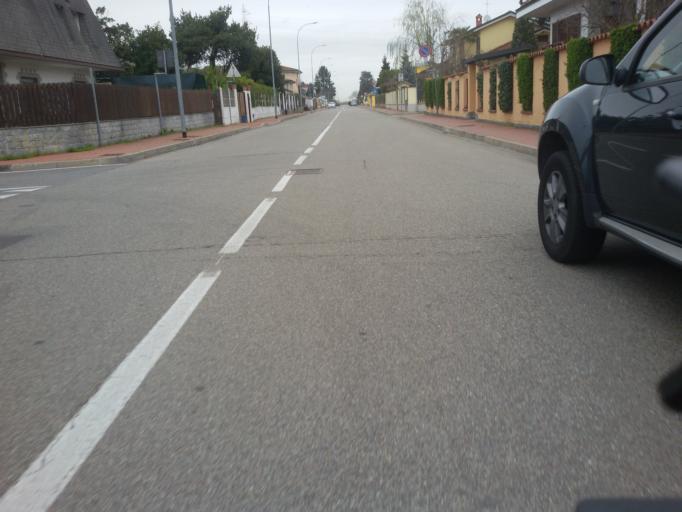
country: IT
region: Lombardy
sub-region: Citta metropolitana di Milano
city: Noviglio
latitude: 45.3592
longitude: 9.0522
